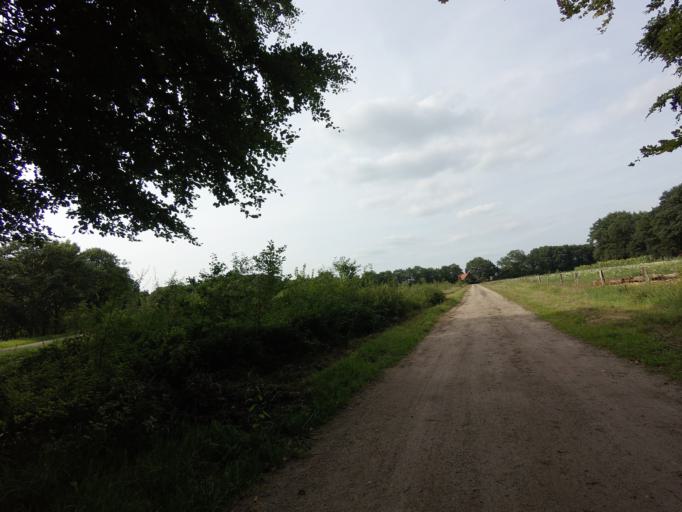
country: DE
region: Lower Saxony
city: Getelo
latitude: 52.4498
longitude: 6.8192
